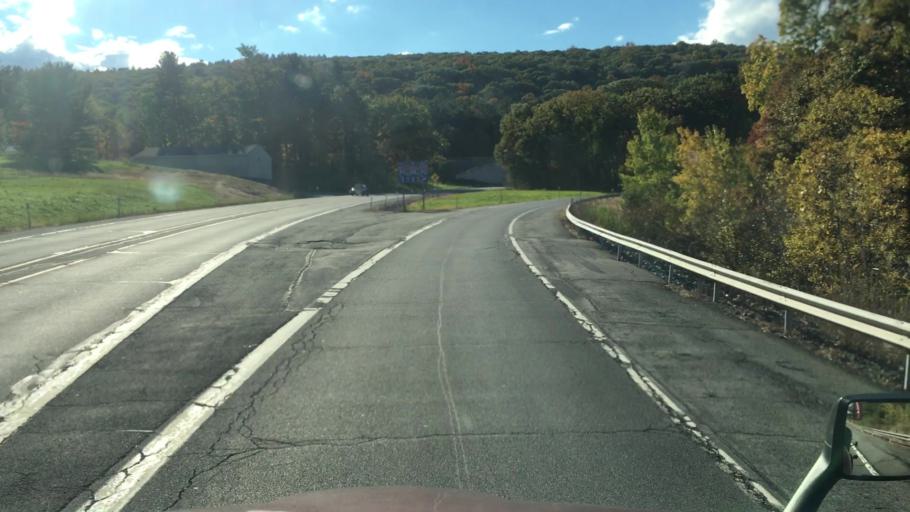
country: US
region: New York
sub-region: Schenectady County
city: Scotia
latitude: 42.8392
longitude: -74.0092
